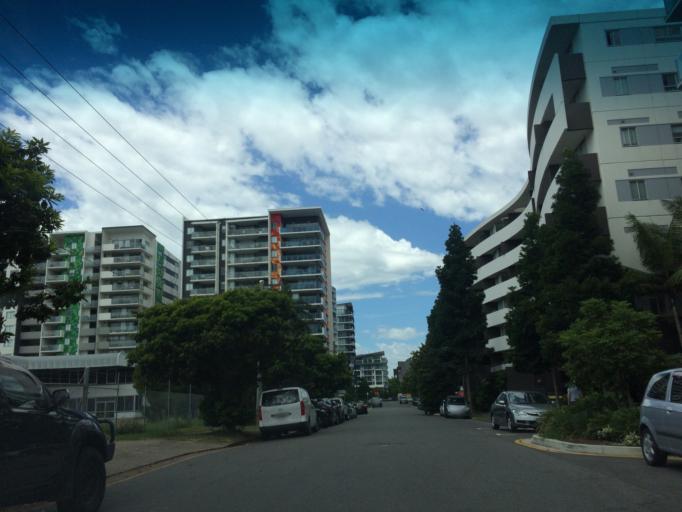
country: AU
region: Queensland
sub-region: Brisbane
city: Toowong
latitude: -27.4832
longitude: 153.0006
